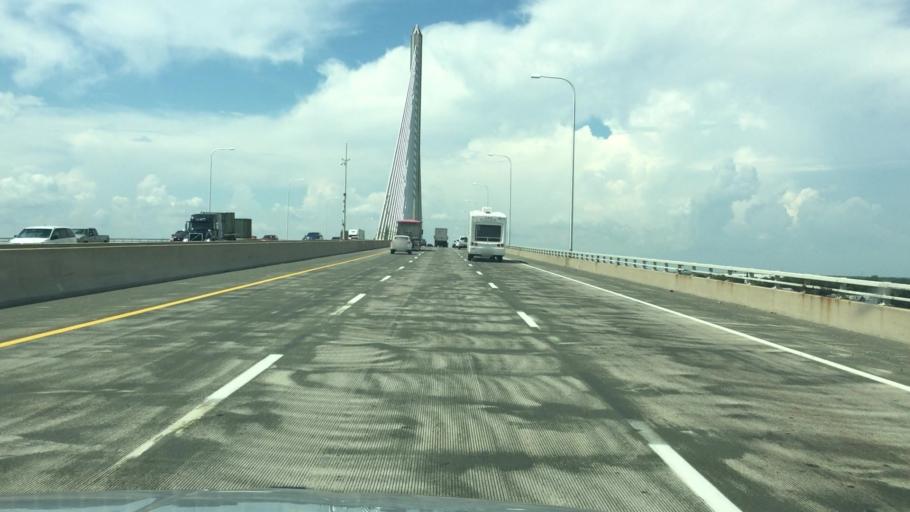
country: US
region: Ohio
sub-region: Lucas County
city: Oregon
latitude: 41.6583
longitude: -83.5096
